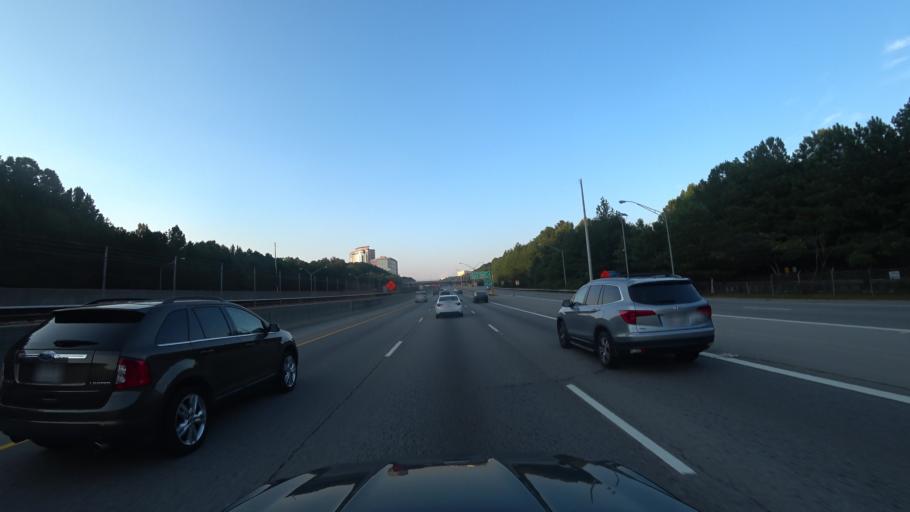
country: US
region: Georgia
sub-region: Fulton County
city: Sandy Springs
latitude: 33.8971
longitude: -84.3626
